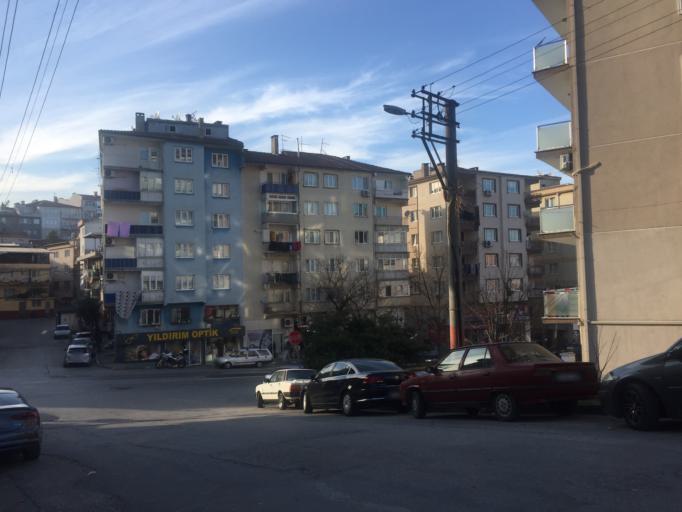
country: TR
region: Bursa
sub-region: Osmangazi
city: Bursa
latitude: 40.1867
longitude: 29.0850
